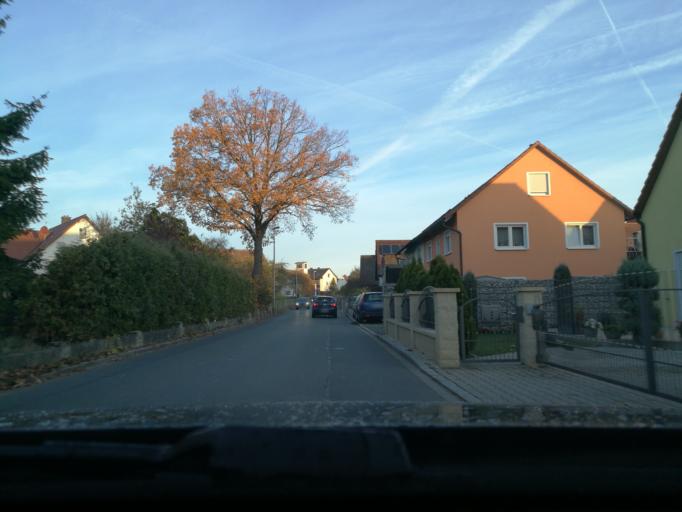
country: DE
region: Bavaria
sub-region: Regierungsbezirk Mittelfranken
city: Herzogenaurach
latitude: 49.5621
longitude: 10.9157
